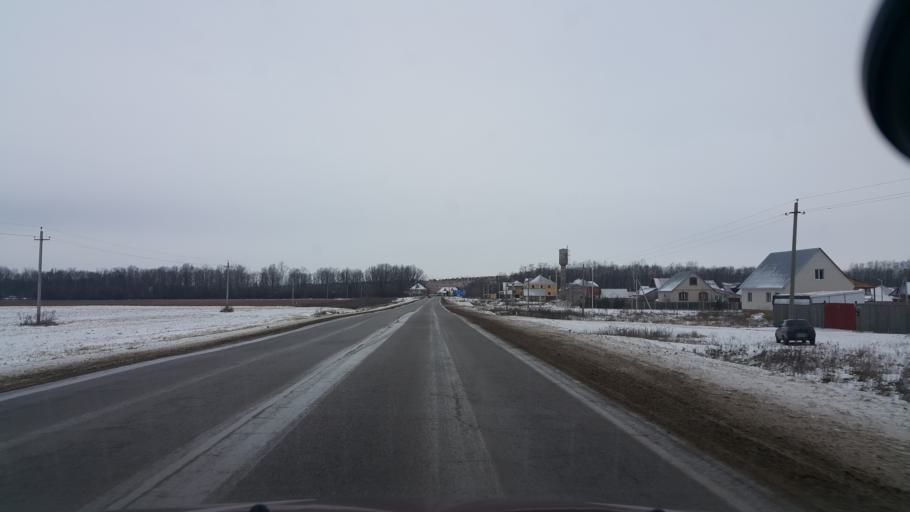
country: RU
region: Tambov
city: Bokino
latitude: 52.6166
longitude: 41.4511
